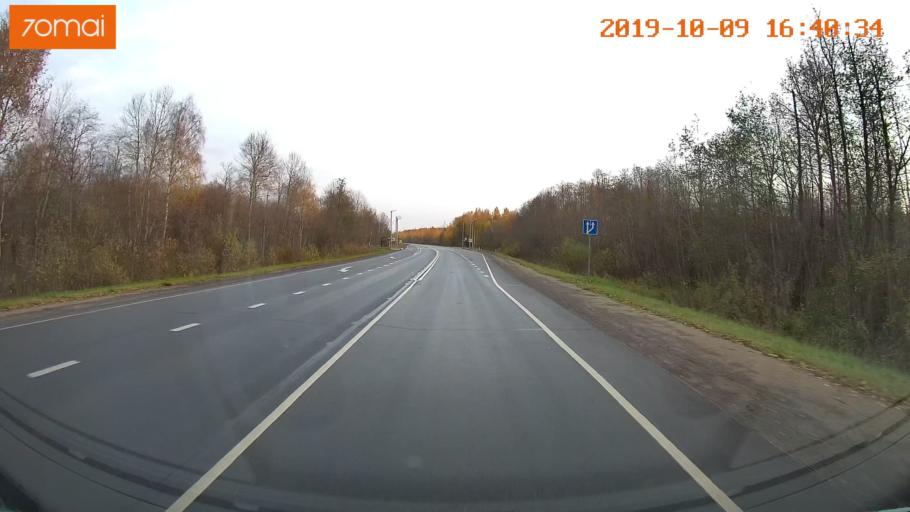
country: RU
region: Kostroma
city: Volgorechensk
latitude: 57.4819
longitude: 41.0629
